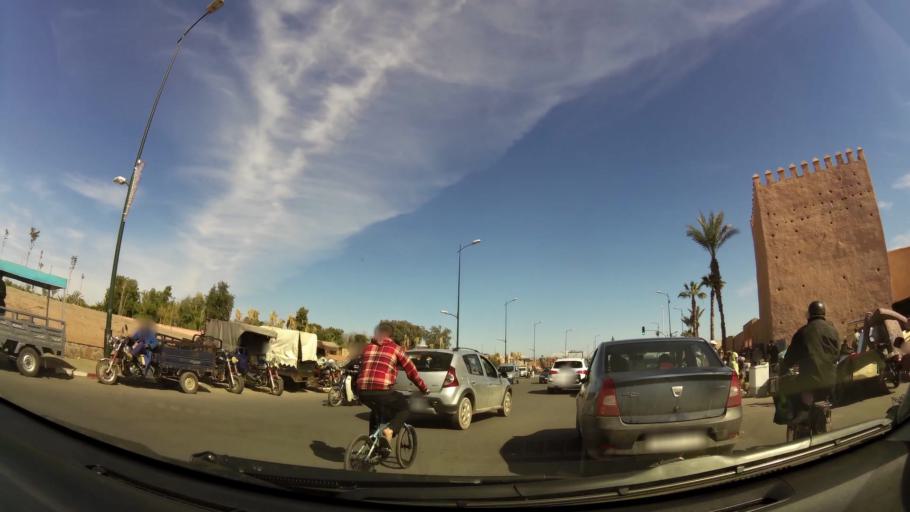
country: MA
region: Marrakech-Tensift-Al Haouz
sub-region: Marrakech
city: Marrakesh
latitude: 31.6405
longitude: -7.9835
